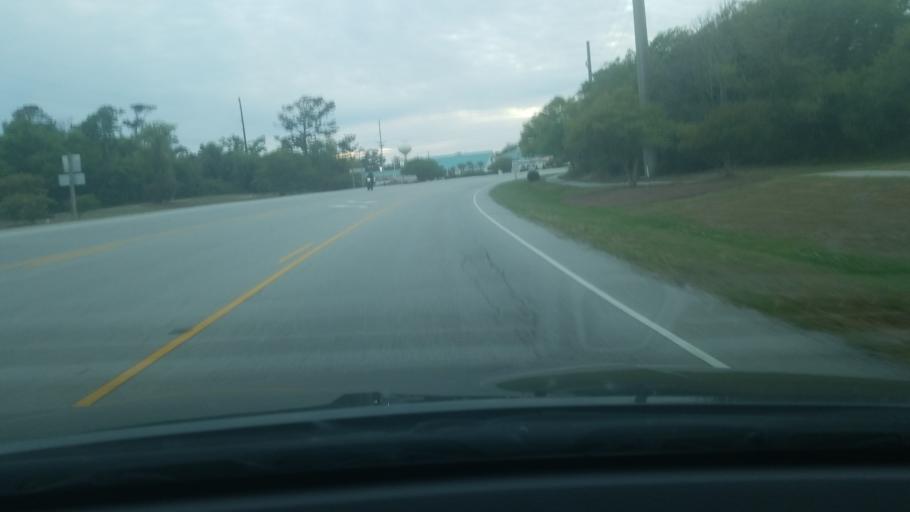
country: US
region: North Carolina
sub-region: Carteret County
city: Cedar Point
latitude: 34.6603
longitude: -77.0565
